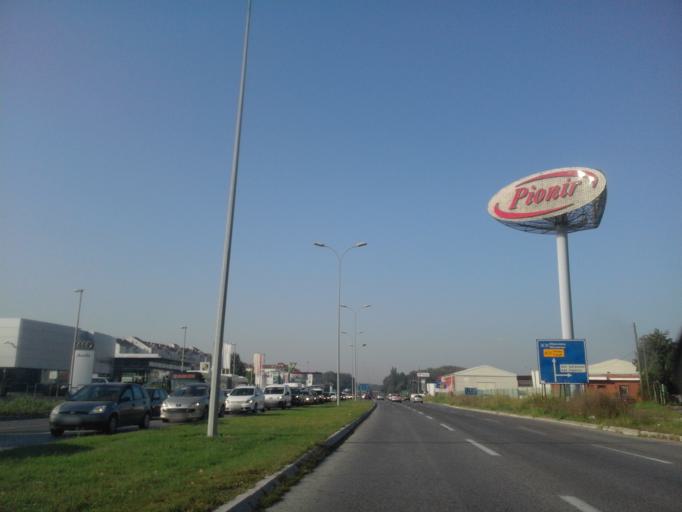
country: RS
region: Central Serbia
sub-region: Belgrade
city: Cukarica
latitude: 44.7859
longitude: 20.4139
